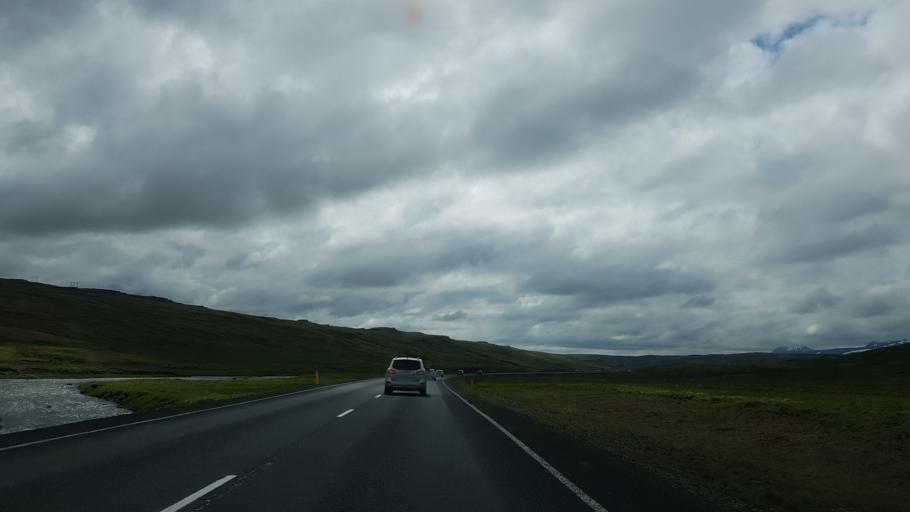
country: IS
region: West
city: Borgarnes
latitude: 64.9210
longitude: -21.1237
